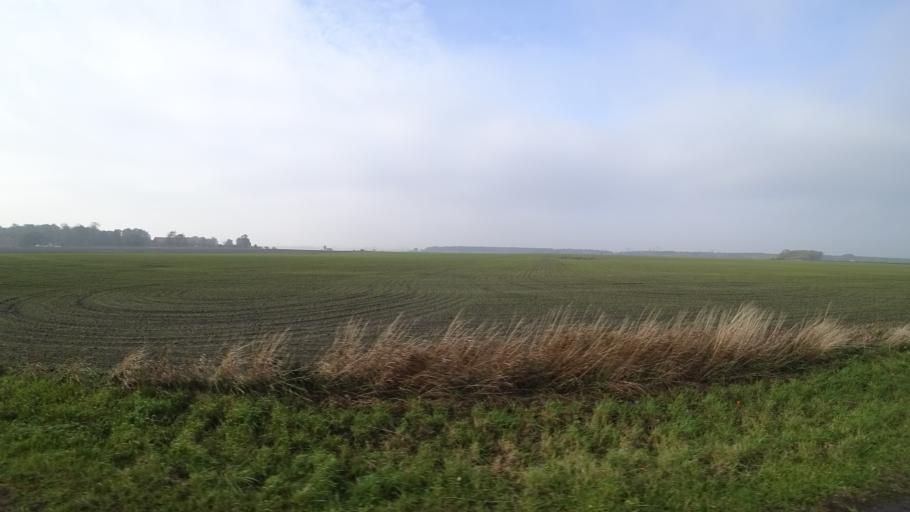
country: SE
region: Skane
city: Bjarred
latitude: 55.7362
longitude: 12.9833
